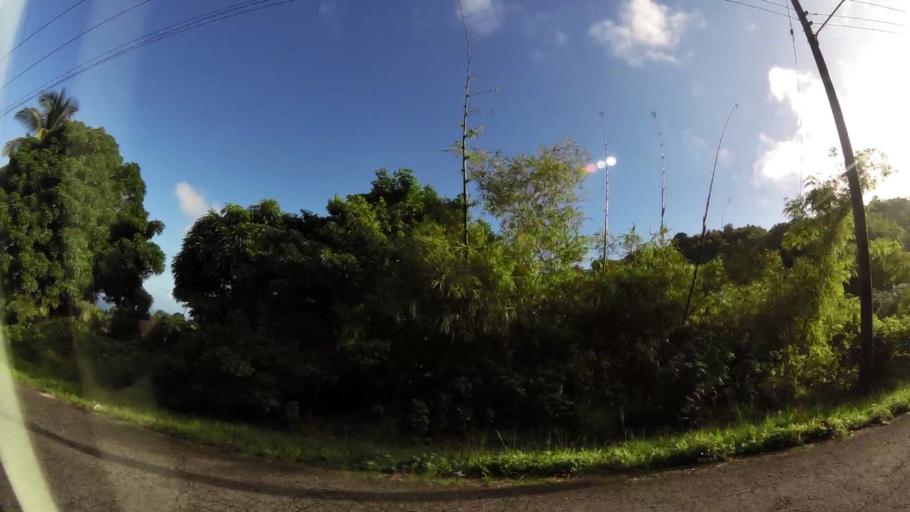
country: LC
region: Anse-la-Raye
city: Canaries
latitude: 13.9149
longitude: -61.0485
